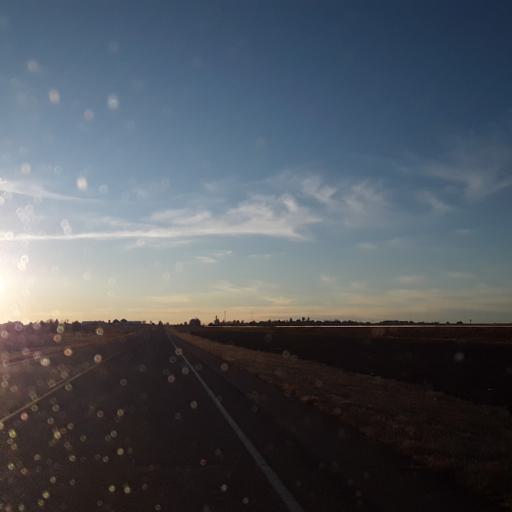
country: US
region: Colorado
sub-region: Cheyenne County
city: Cheyenne Wells
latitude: 38.8259
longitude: -102.3200
